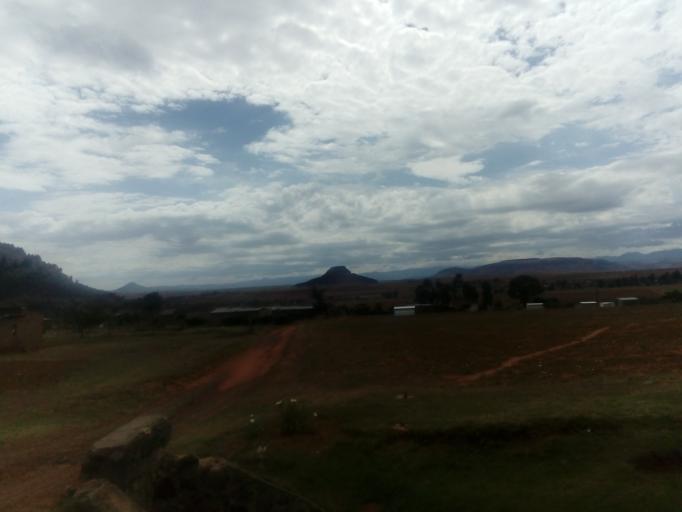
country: LS
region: Leribe
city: Maputsoe
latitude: -28.9618
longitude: 27.9616
